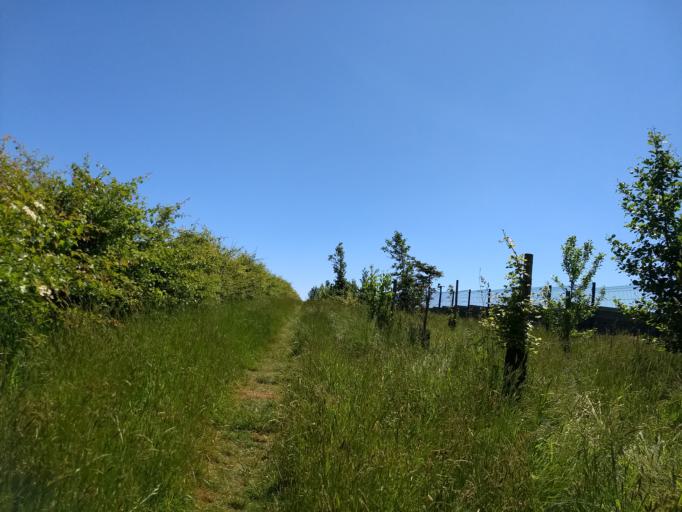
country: GB
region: England
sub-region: Isle of Wight
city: Seaview
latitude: 50.7026
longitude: -1.1214
